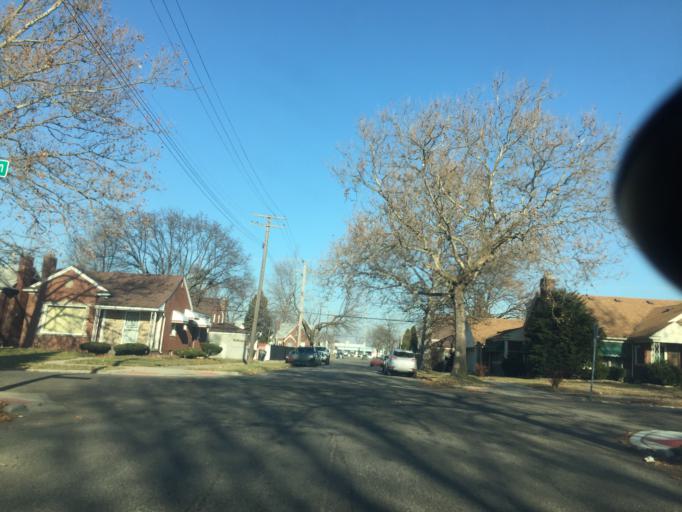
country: US
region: Michigan
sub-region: Macomb County
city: Eastpointe
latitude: 42.4480
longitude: -82.9636
